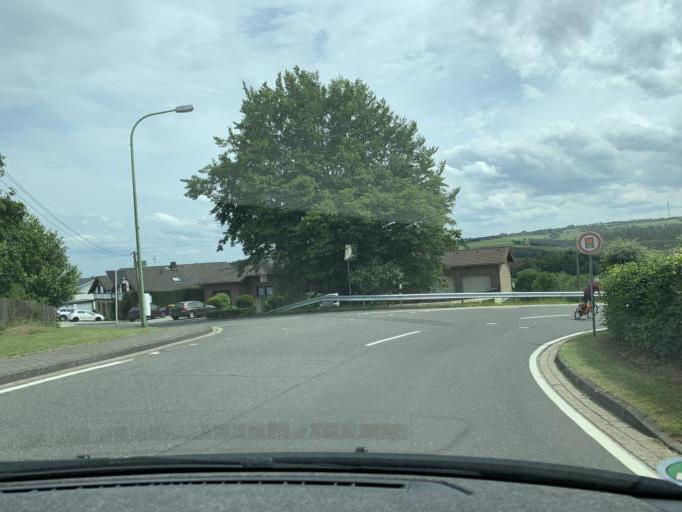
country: DE
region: North Rhine-Westphalia
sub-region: Regierungsbezirk Koln
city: Hurtgenwald
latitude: 50.6894
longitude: 6.3864
